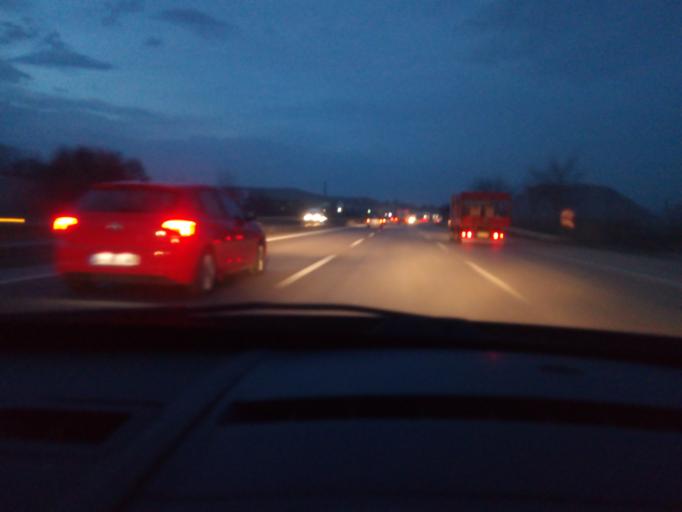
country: TR
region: Balikesir
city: Susurluk
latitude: 39.9605
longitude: 28.1706
